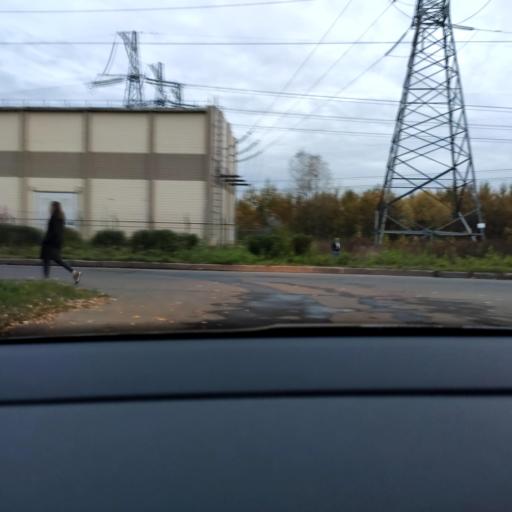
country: RU
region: Moscow
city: Bibirevo
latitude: 55.8886
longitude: 37.6209
